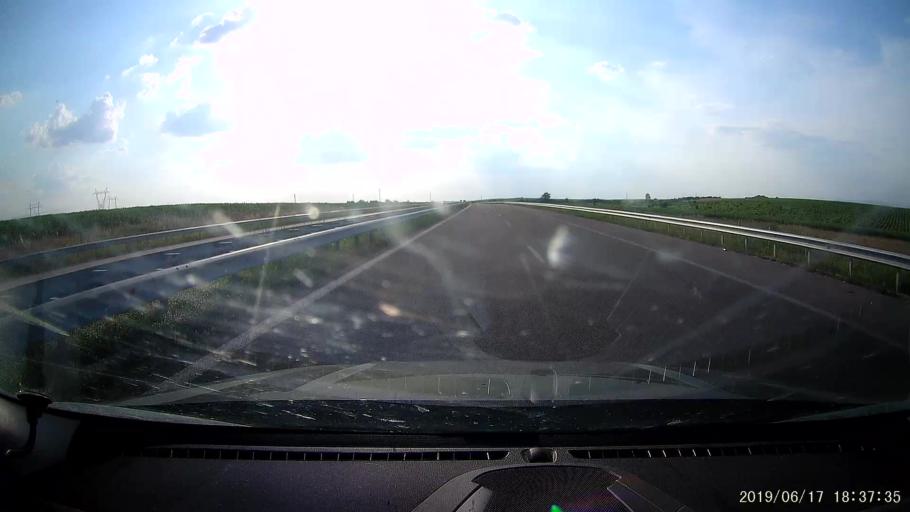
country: BG
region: Stara Zagora
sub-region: Obshtina Chirpan
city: Chirpan
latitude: 42.1319
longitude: 25.3571
